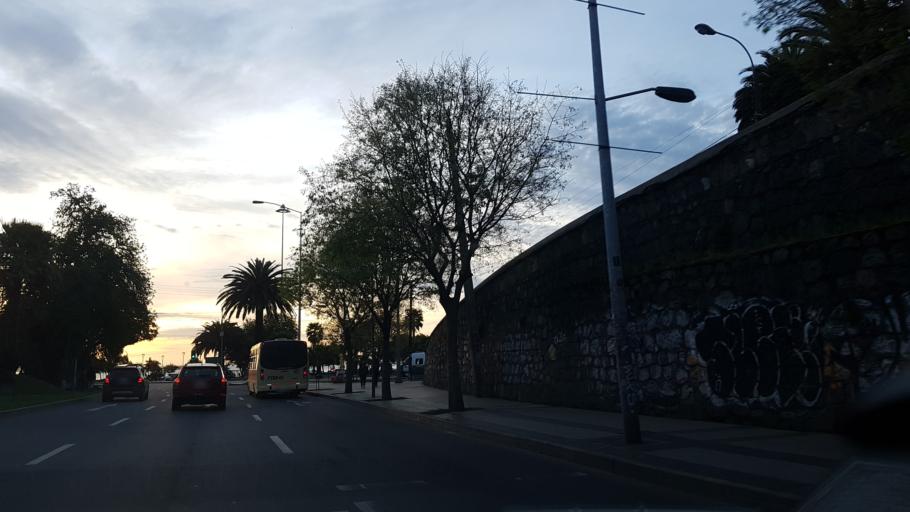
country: CL
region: Valparaiso
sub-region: Provincia de Valparaiso
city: Vina del Mar
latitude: -33.0239
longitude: -71.5665
